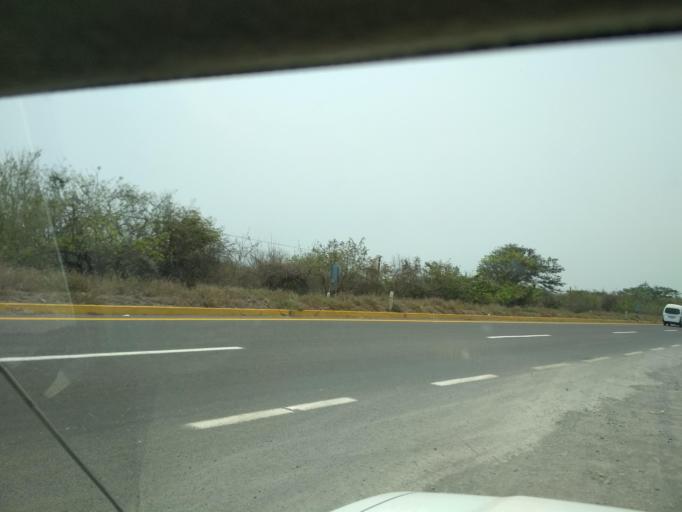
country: MX
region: Veracruz
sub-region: Veracruz
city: Delfino Victoria (Santa Fe)
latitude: 19.2167
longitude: -96.2582
